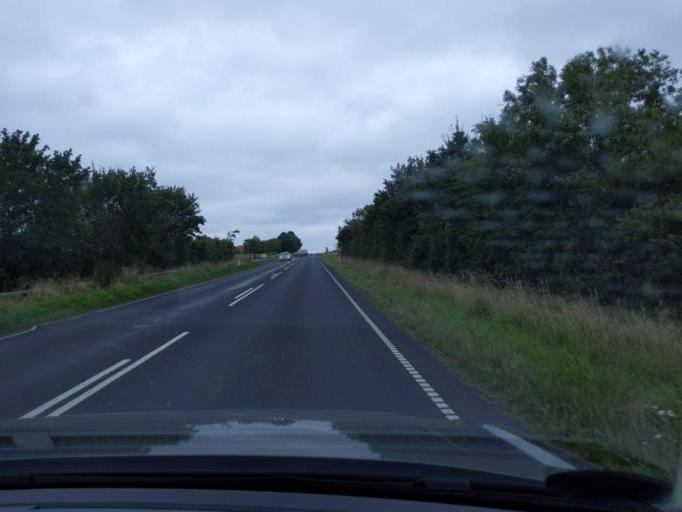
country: DK
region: Central Jutland
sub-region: Randers Kommune
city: Spentrup
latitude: 56.5206
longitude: 9.9370
